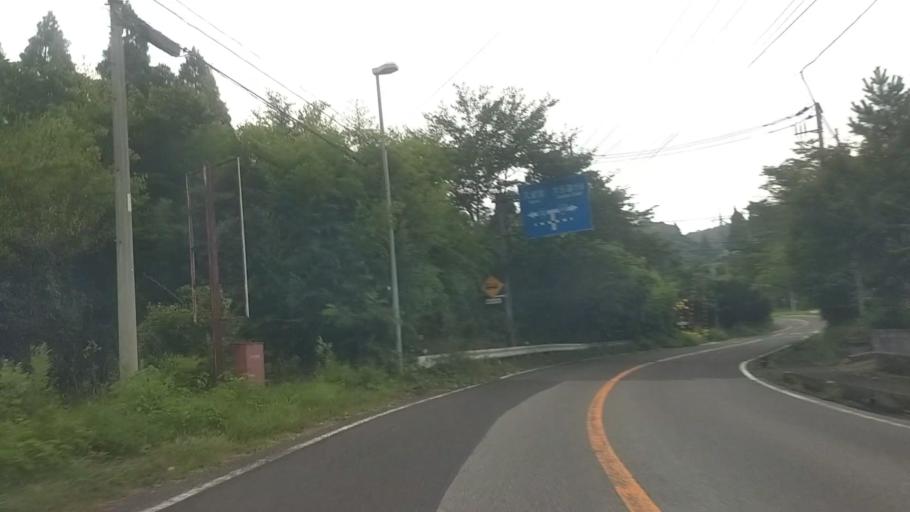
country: JP
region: Chiba
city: Katsuura
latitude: 35.2505
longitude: 140.1954
